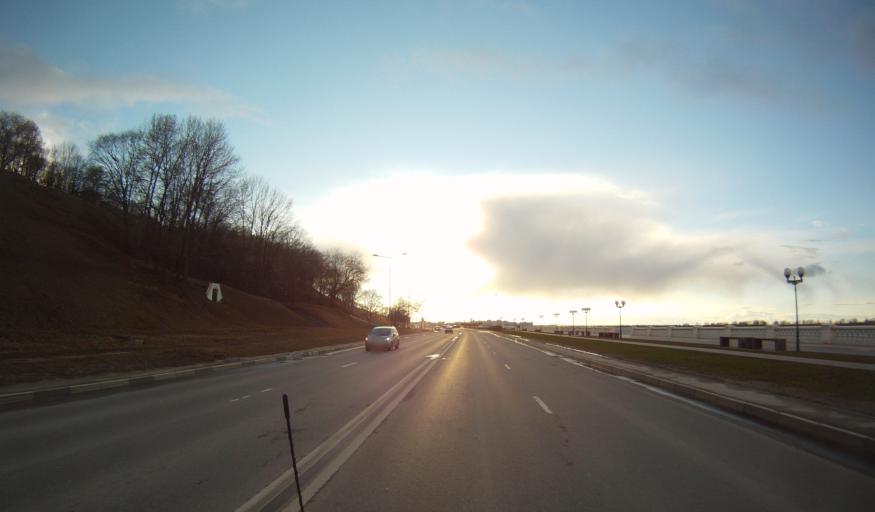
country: RU
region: Nizjnij Novgorod
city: Nizhniy Novgorod
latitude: 56.3315
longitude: 44.0163
